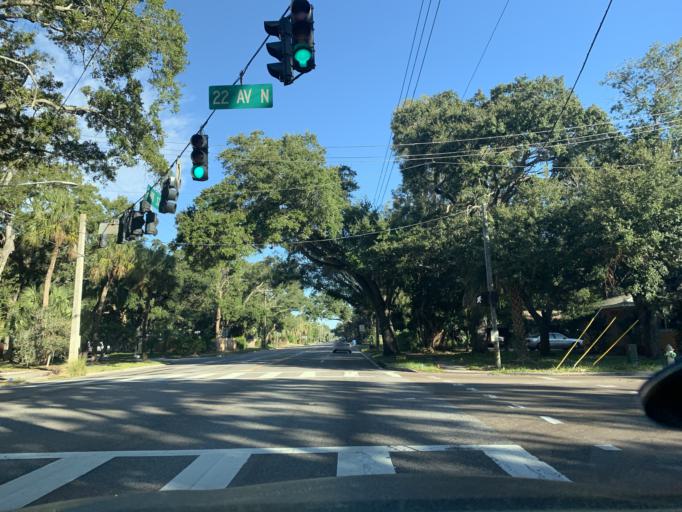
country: US
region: Florida
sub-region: Pinellas County
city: Treasure Island
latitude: 27.7921
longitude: -82.7538
